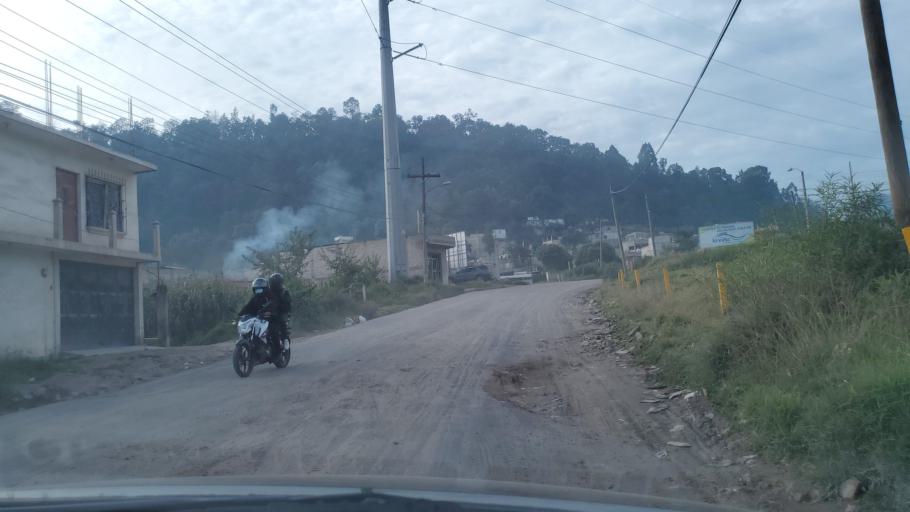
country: GT
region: Quetzaltenango
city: Quetzaltenango
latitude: 14.8263
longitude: -91.5360
